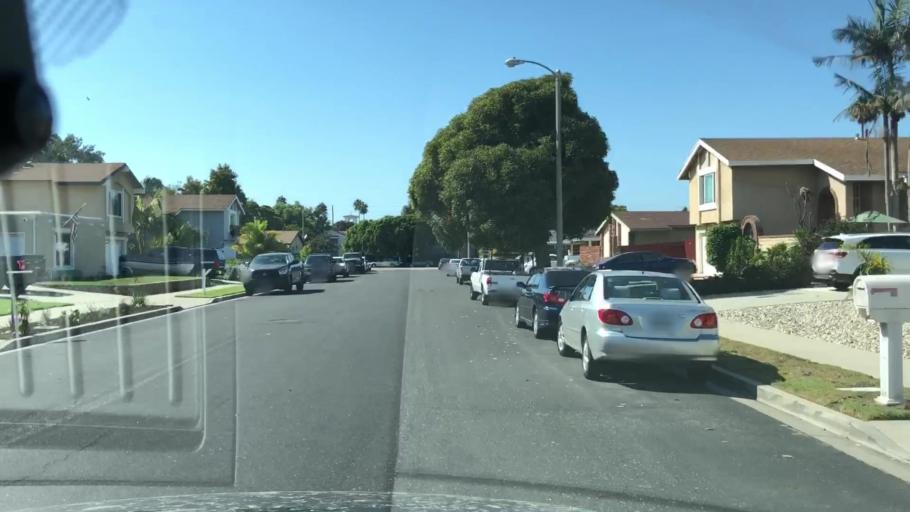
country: US
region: California
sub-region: Ventura County
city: Oxnard Shores
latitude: 34.1874
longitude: -119.2185
